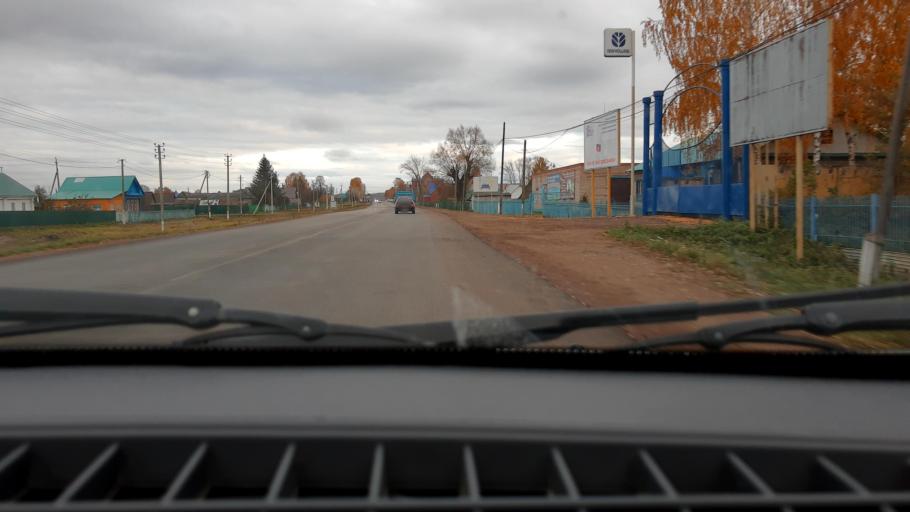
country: RU
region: Bashkortostan
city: Ulukulevo
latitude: 54.4340
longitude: 56.3187
